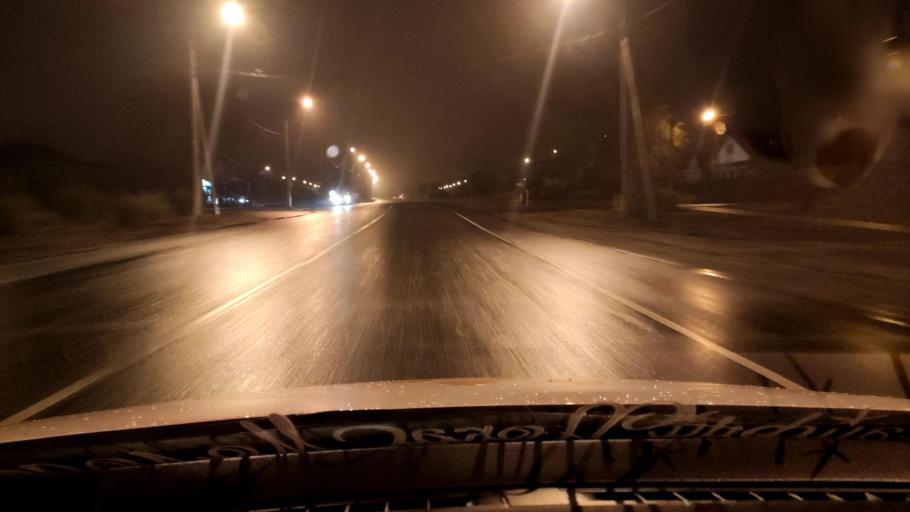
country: RU
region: Voronezj
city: Pridonskoy
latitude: 51.7046
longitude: 39.0759
